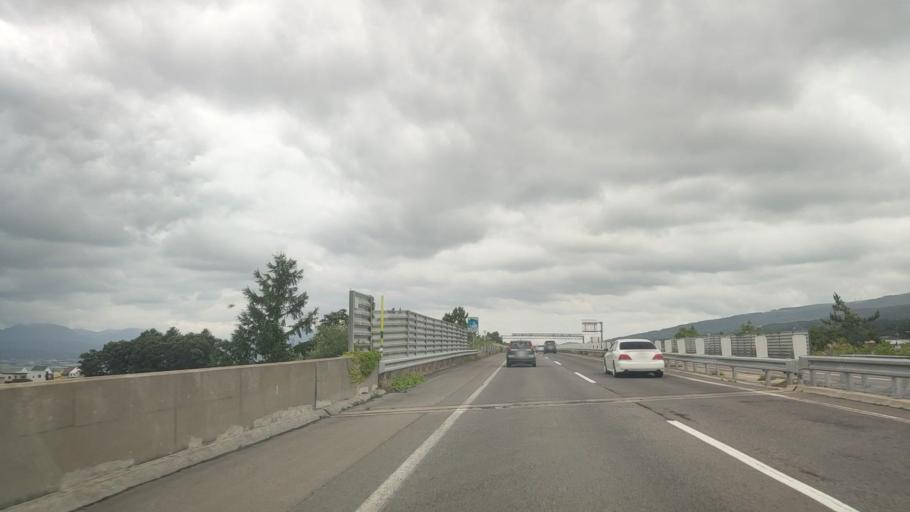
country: JP
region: Hokkaido
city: Nanae
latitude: 41.8590
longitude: 140.7350
